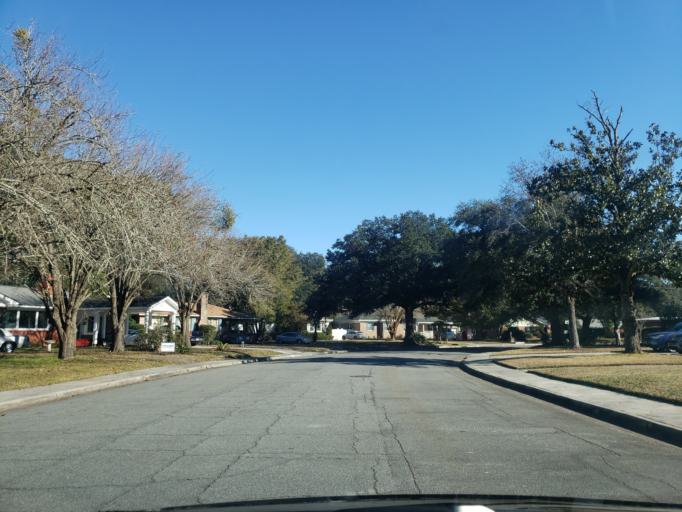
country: US
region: Georgia
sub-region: Chatham County
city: Thunderbolt
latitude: 32.0234
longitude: -81.0985
